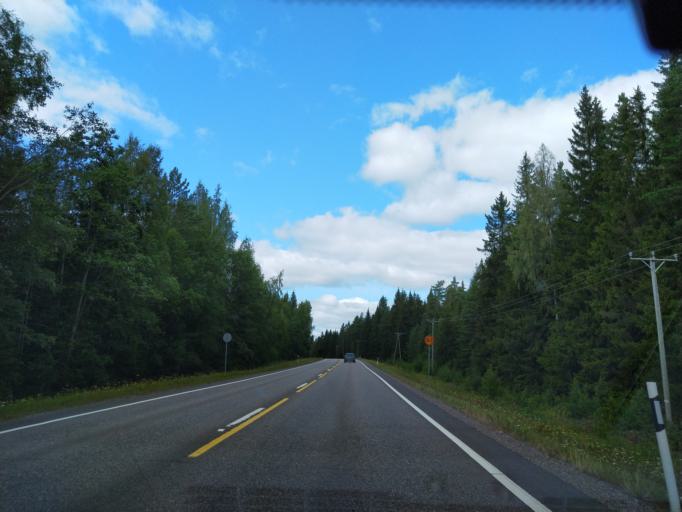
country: FI
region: Haeme
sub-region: Haemeenlinna
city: Renko
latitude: 60.7581
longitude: 24.2954
